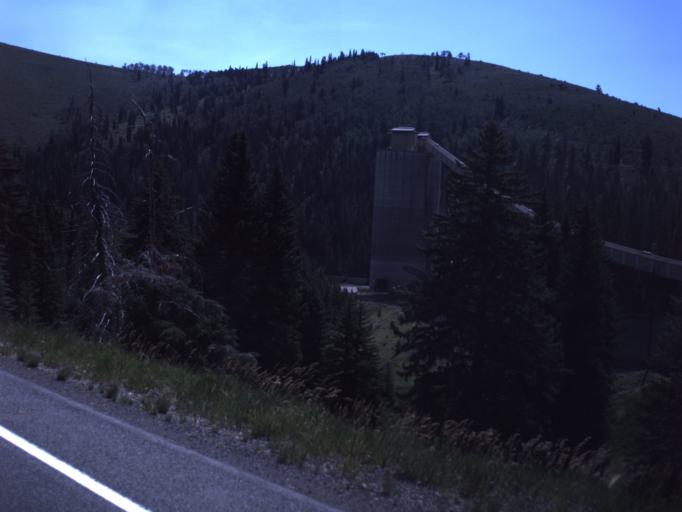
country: US
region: Utah
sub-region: Sanpete County
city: Fairview
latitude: 39.6853
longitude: -111.1618
